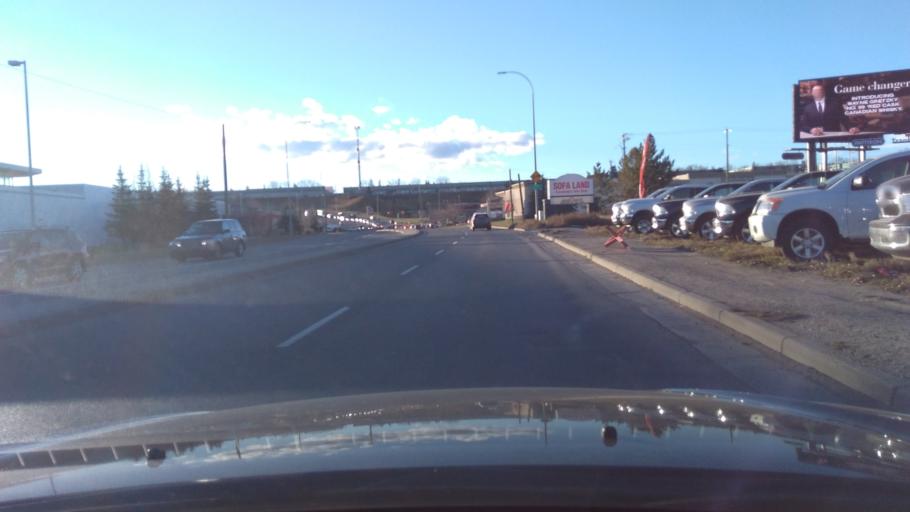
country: CA
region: Alberta
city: Calgary
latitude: 50.9873
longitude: -114.0403
